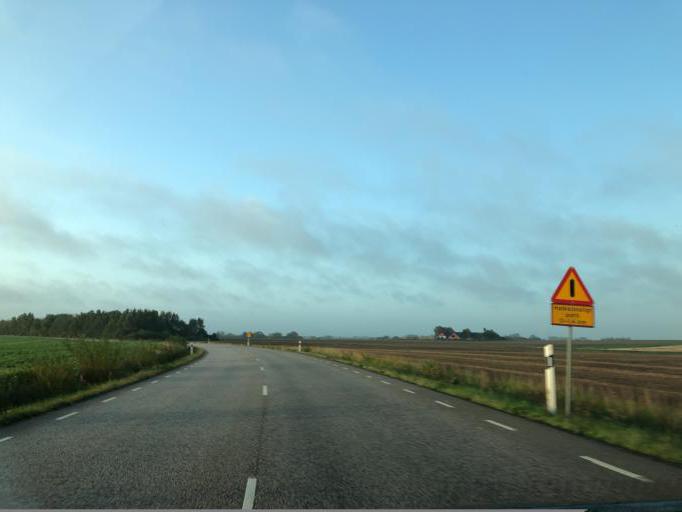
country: SE
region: Skane
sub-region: Kavlinge Kommun
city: Kaevlinge
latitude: 55.7678
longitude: 13.1052
